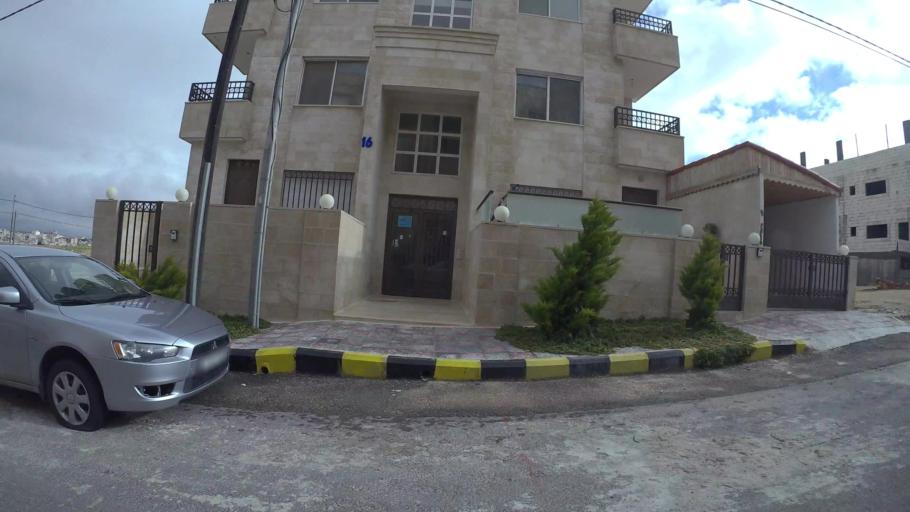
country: JO
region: Amman
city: Al Jubayhah
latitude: 32.0634
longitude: 35.8877
